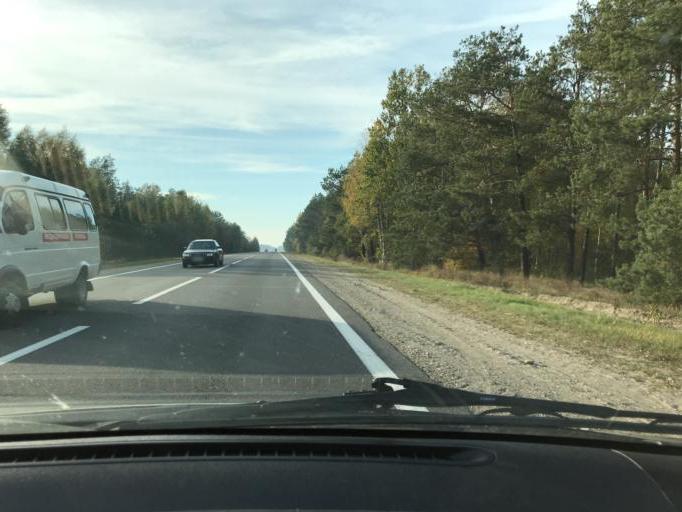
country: BY
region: Brest
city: Horad Pinsk
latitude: 52.1484
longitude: 25.8900
